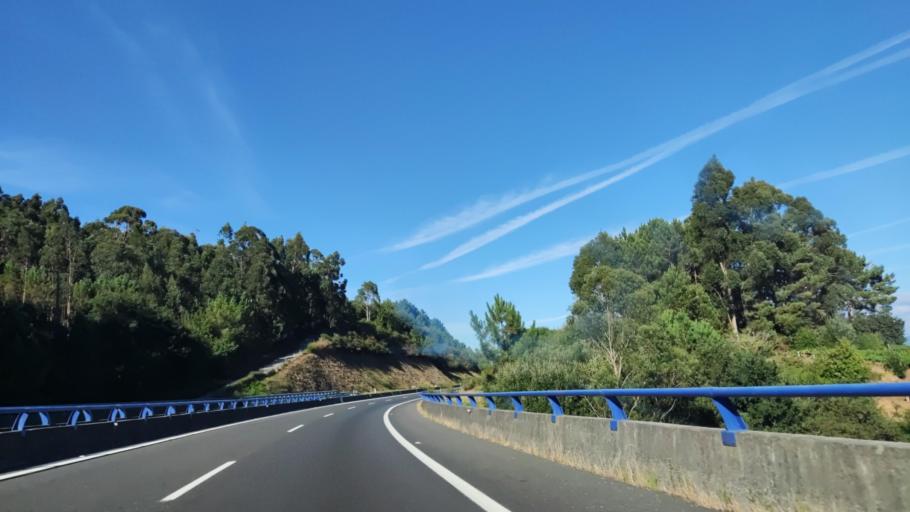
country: ES
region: Galicia
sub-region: Provincia da Coruna
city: Boiro
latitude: 42.6442
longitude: -8.9100
